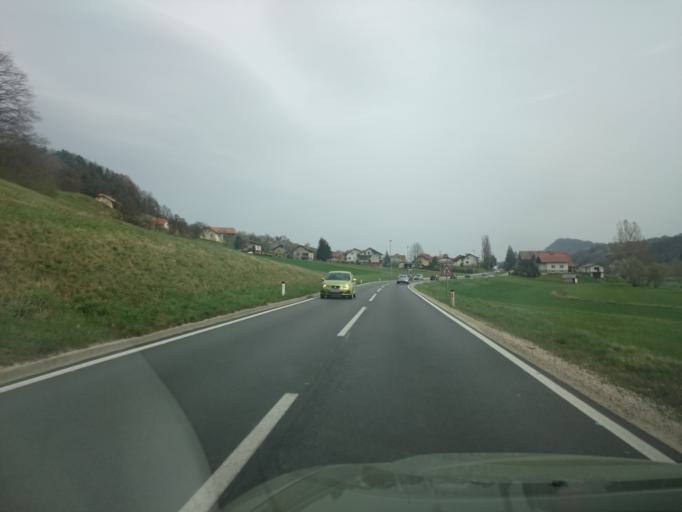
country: SI
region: Store
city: Store
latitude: 46.2206
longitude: 15.3464
